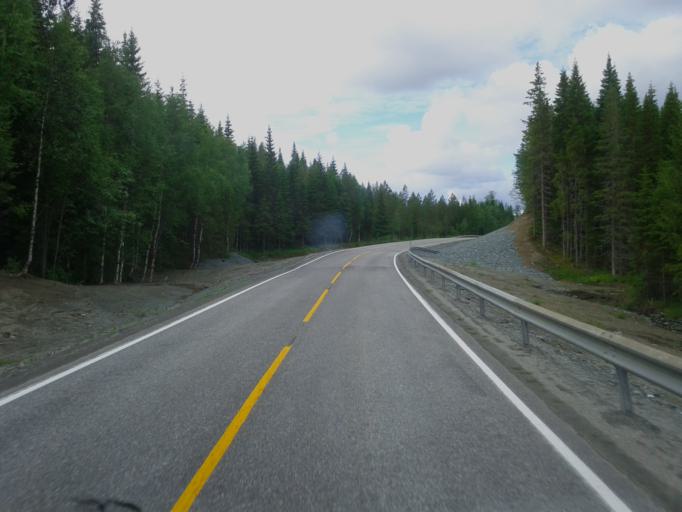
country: NO
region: Nord-Trondelag
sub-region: Hoylandet
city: Hoylandet
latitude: 64.6634
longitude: 12.6639
